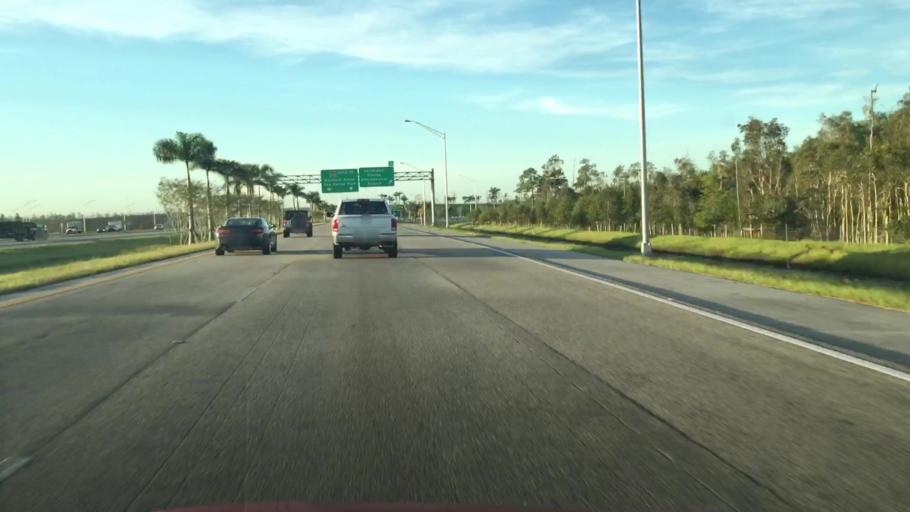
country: US
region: Florida
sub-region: Lee County
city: Three Oaks
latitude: 26.5174
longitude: -81.7957
